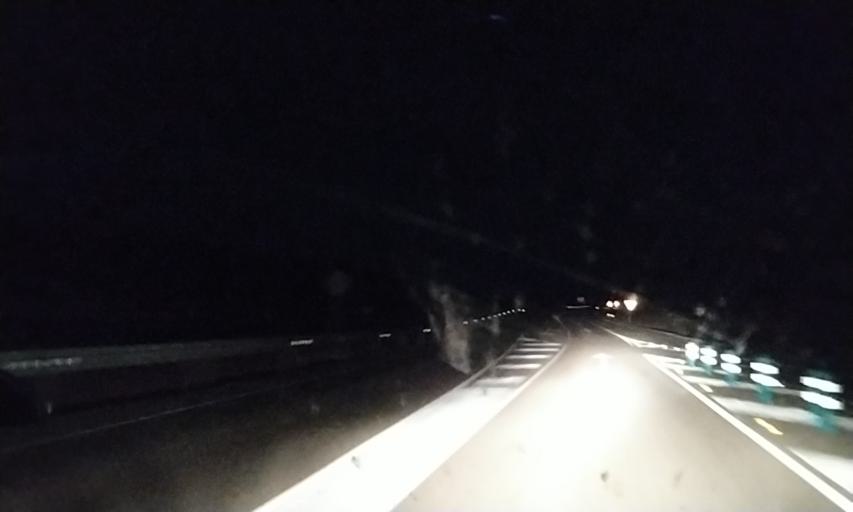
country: ES
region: Castille and Leon
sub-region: Provincia de Salamanca
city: Herguijuela de Ciudad Rodrigo
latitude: 40.4937
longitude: -6.5798
